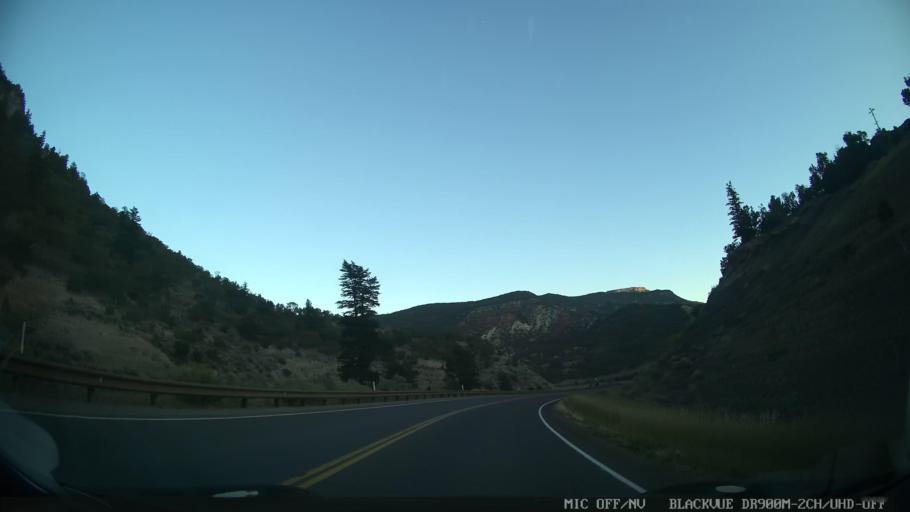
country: US
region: Colorado
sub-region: Eagle County
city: Edwards
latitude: 39.8531
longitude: -106.6457
